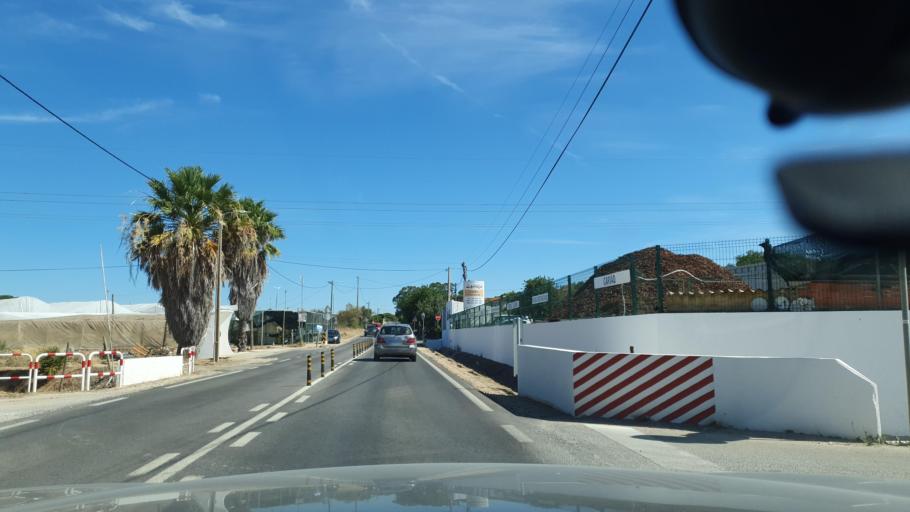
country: PT
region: Faro
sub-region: Albufeira
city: Guia
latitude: 37.1096
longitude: -8.3068
